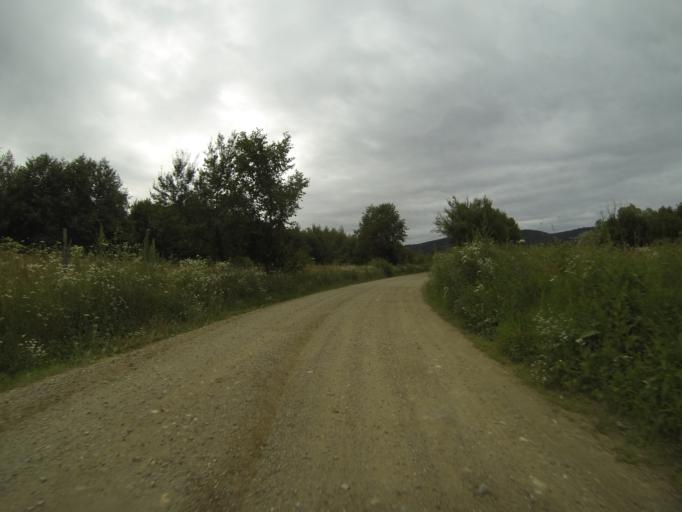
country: RO
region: Brasov
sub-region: Comuna Sinca Noua
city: Sinca Noua
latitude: 45.7269
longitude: 25.2231
